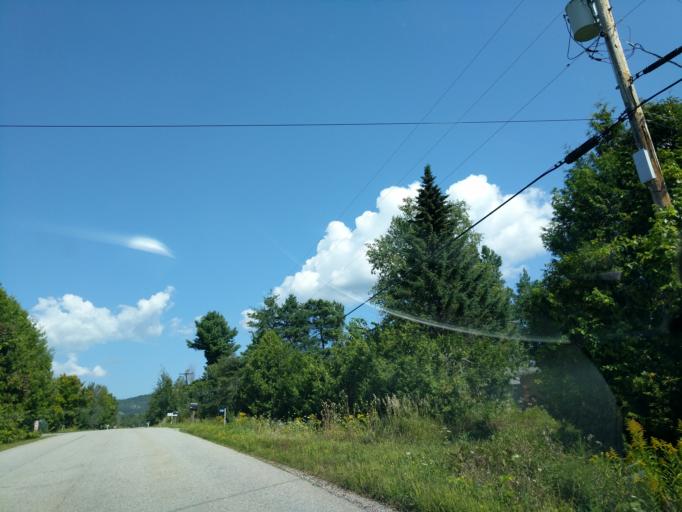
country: CA
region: Quebec
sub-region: Outaouais
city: Wakefield
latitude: 45.4995
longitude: -75.9528
